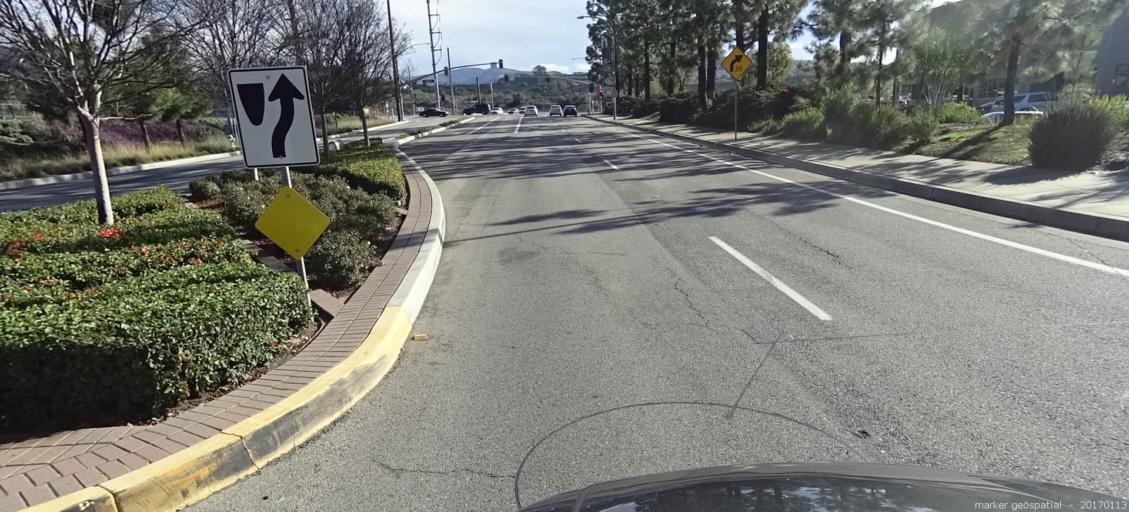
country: US
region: California
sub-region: Orange County
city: Yorba Linda
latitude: 33.9183
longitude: -117.8493
